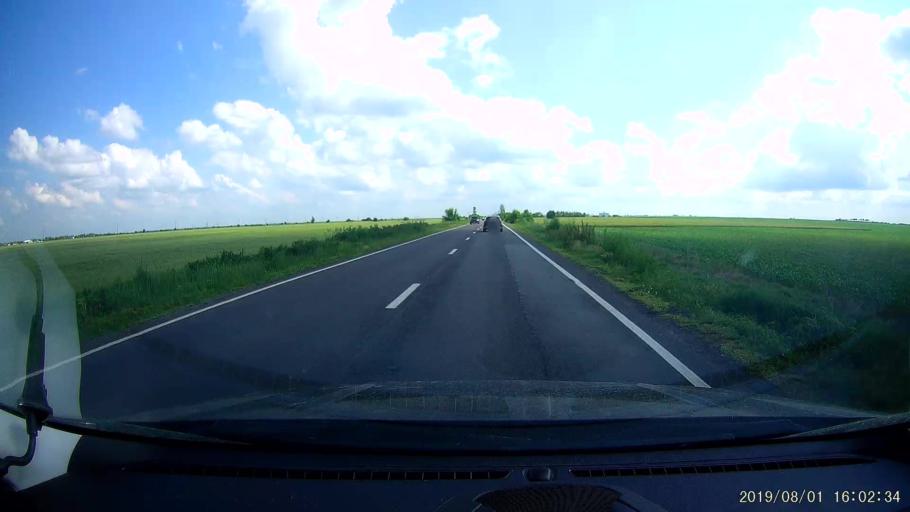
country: RO
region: Ialomita
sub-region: Comuna Ciulnita
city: Ciulnita
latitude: 44.4875
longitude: 27.3870
